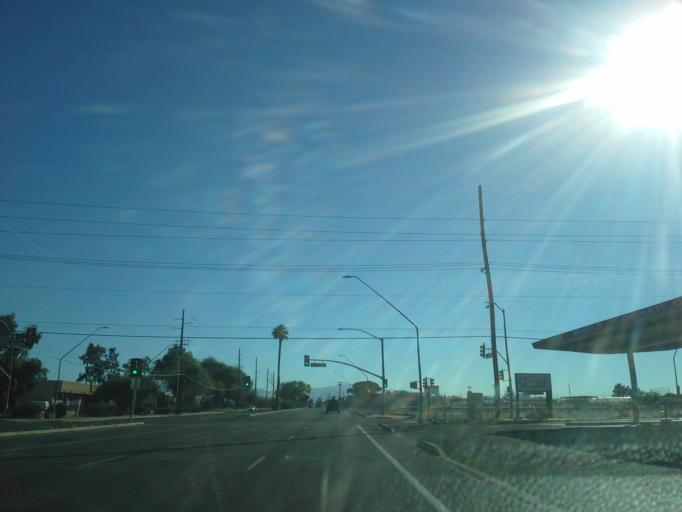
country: US
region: Arizona
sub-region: Pima County
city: Drexel Heights
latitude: 32.1339
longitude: -110.9688
